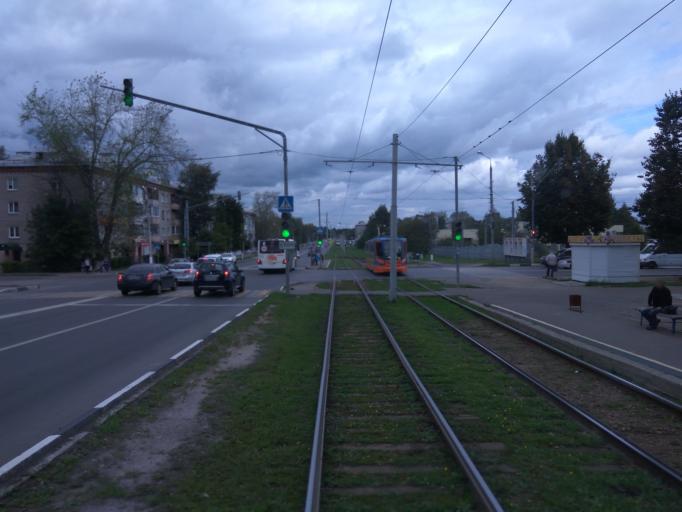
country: RU
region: Moskovskaya
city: Kolomna
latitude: 55.0873
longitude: 38.7654
